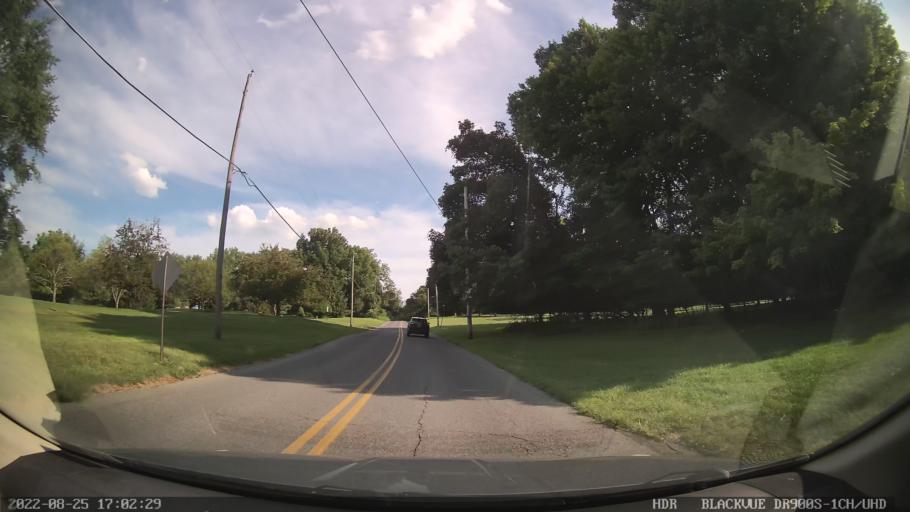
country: US
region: Pennsylvania
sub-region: Lehigh County
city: Emmaus
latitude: 40.5523
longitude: -75.5017
